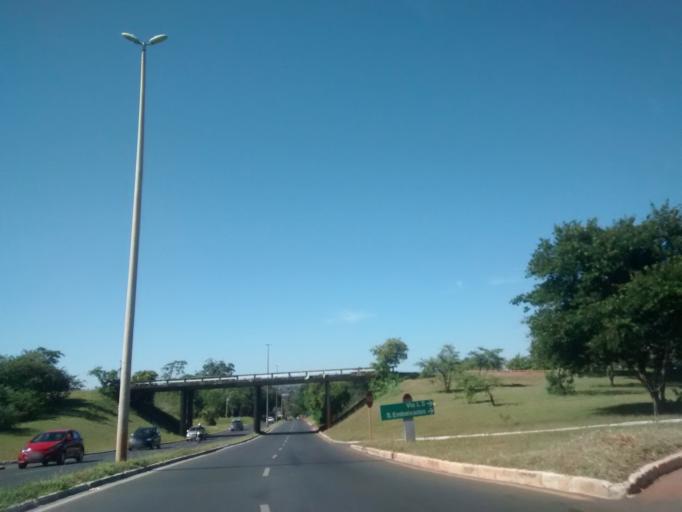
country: BR
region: Federal District
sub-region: Brasilia
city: Brasilia
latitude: -15.8302
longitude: -47.9021
